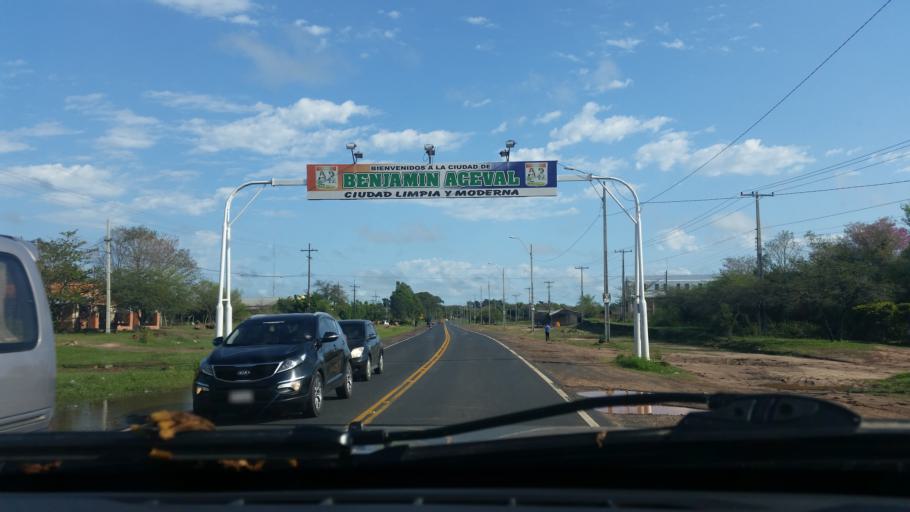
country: PY
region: Presidente Hayes
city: Villa Hayes
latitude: -25.0471
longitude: -57.5428
